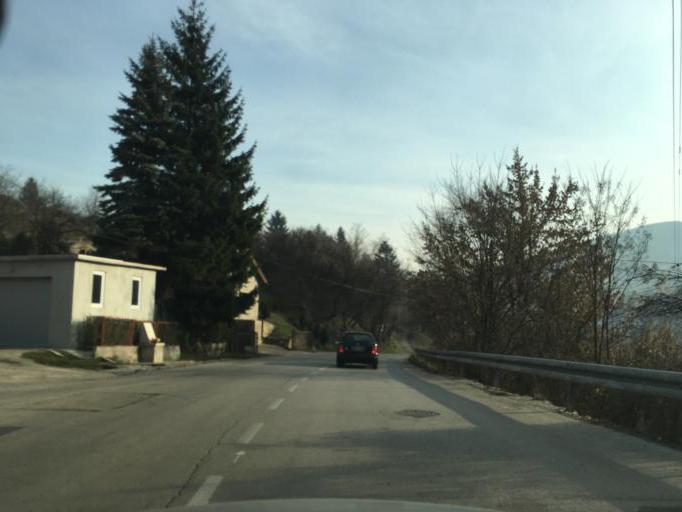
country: BA
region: Federation of Bosnia and Herzegovina
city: Zenica
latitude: 44.1931
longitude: 17.8831
